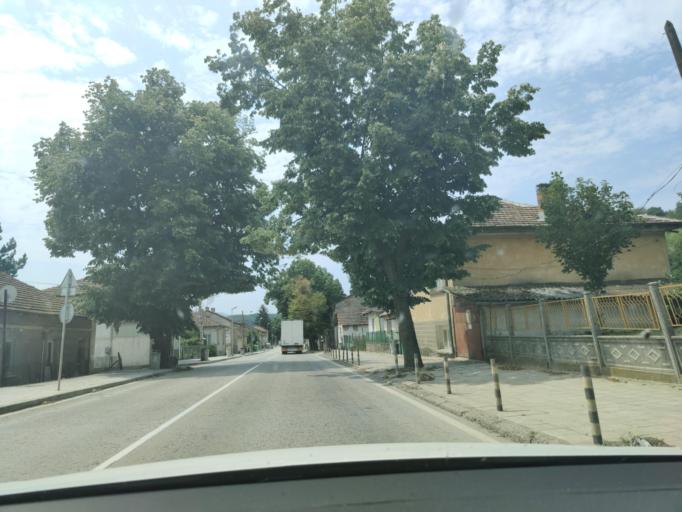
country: BG
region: Vidin
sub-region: Obshtina Dimovo
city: Dimovo
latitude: 43.7454
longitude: 22.7306
